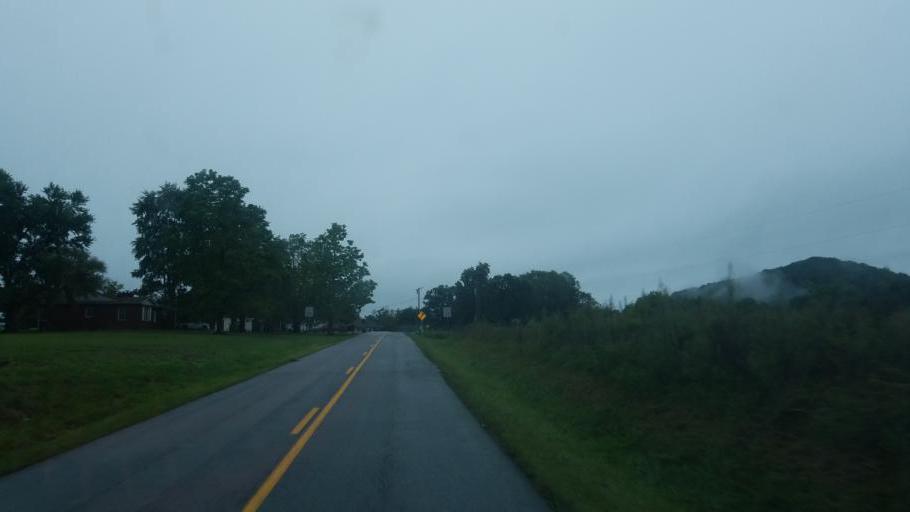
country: US
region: Kentucky
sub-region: Fleming County
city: Flemingsburg
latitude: 38.4042
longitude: -83.6077
